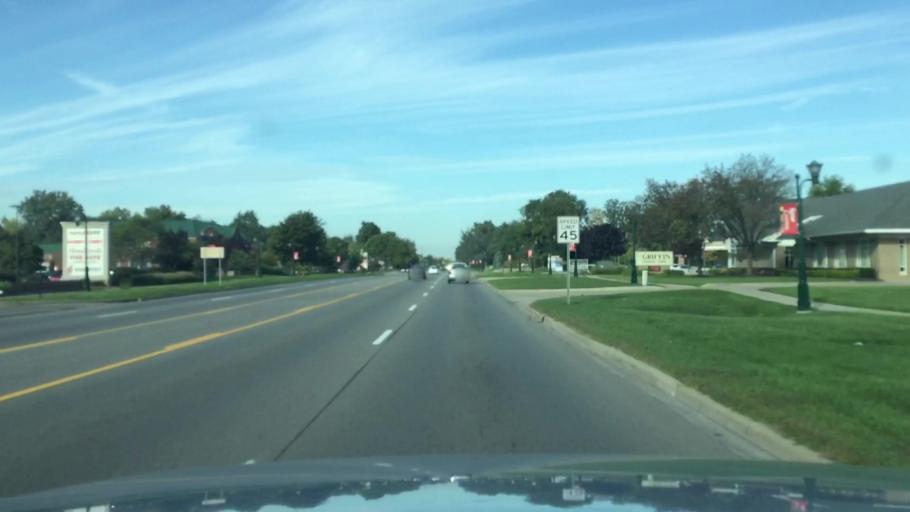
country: US
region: Michigan
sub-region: Wayne County
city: Canton
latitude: 42.3226
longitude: -83.4600
